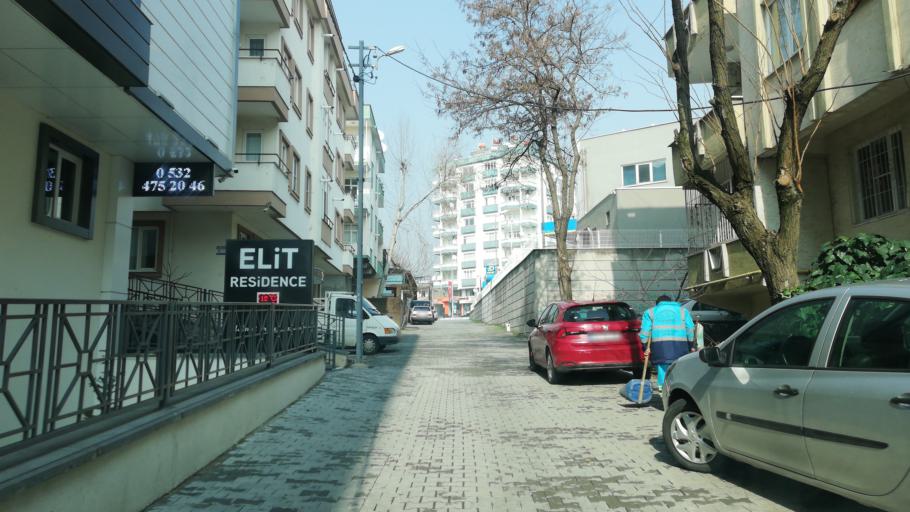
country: TR
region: Kahramanmaras
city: Kahramanmaras
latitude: 37.5721
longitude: 36.9359
